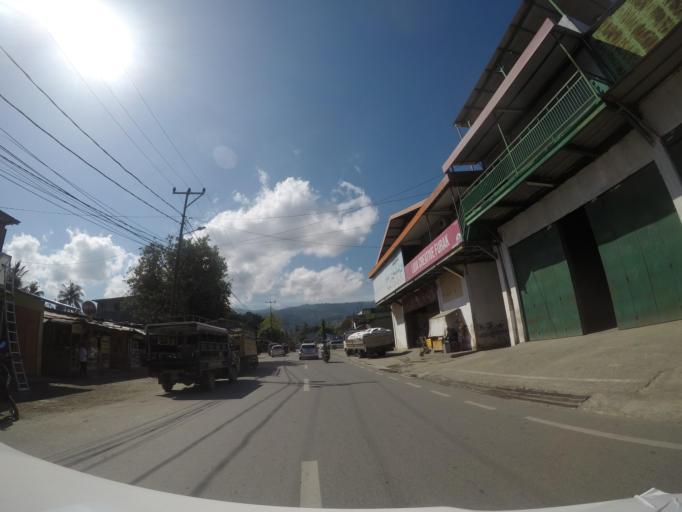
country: TL
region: Dili
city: Dili
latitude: -8.5529
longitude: 125.5907
